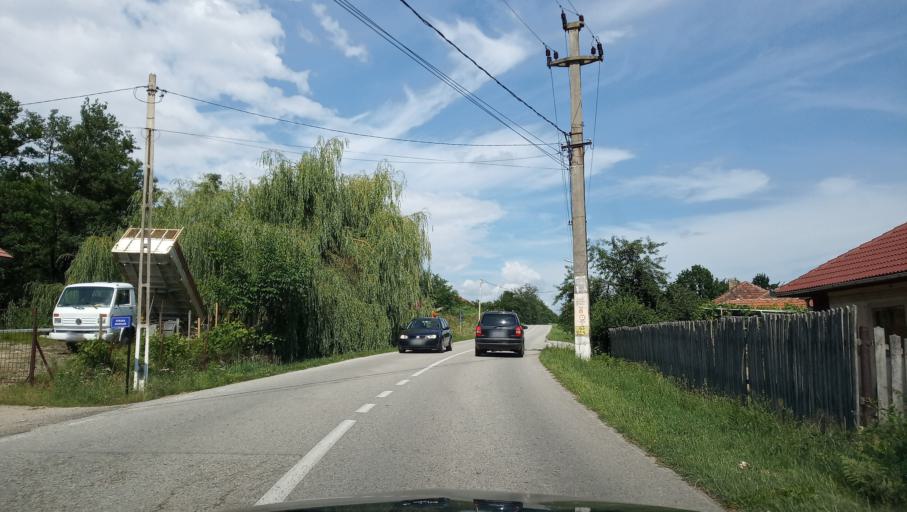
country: RO
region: Gorj
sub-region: Comuna Crasna
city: Carpinis
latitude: 45.1853
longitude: 23.5550
